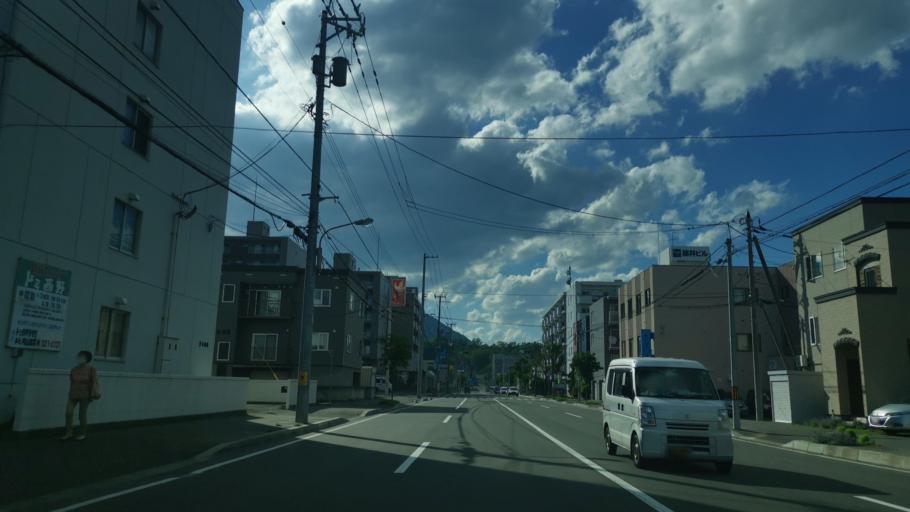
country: JP
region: Hokkaido
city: Sapporo
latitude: 43.0795
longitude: 141.2749
